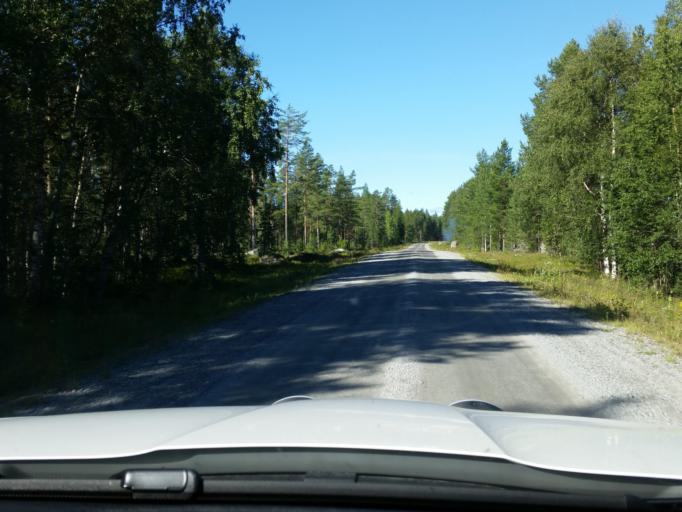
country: SE
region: Norrbotten
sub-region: Pitea Kommun
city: Roknas
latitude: 65.2655
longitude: 21.1747
